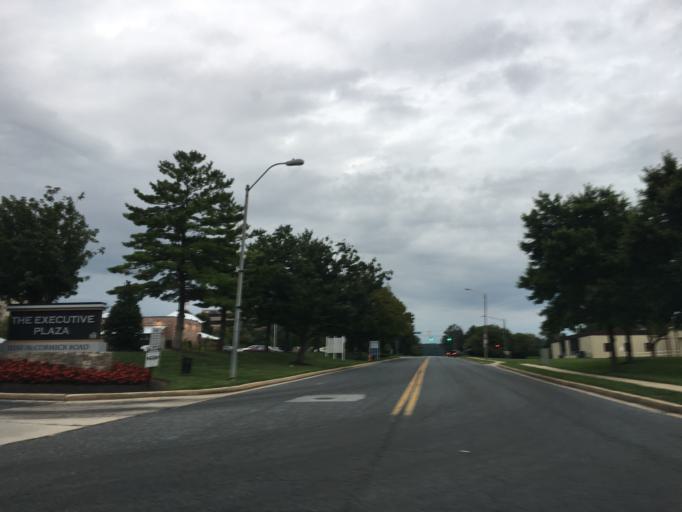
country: US
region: Maryland
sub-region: Baltimore County
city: Cockeysville
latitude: 39.4920
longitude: -76.6607
